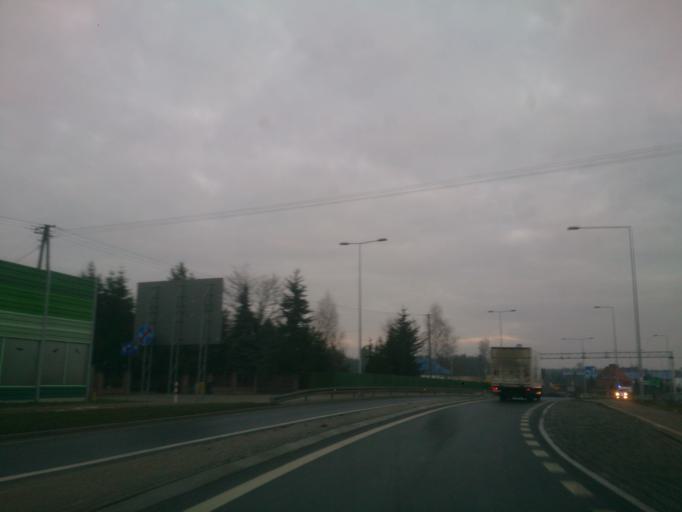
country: PL
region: Kujawsko-Pomorskie
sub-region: Grudziadz
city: Grudziadz
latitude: 53.5001
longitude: 18.6811
